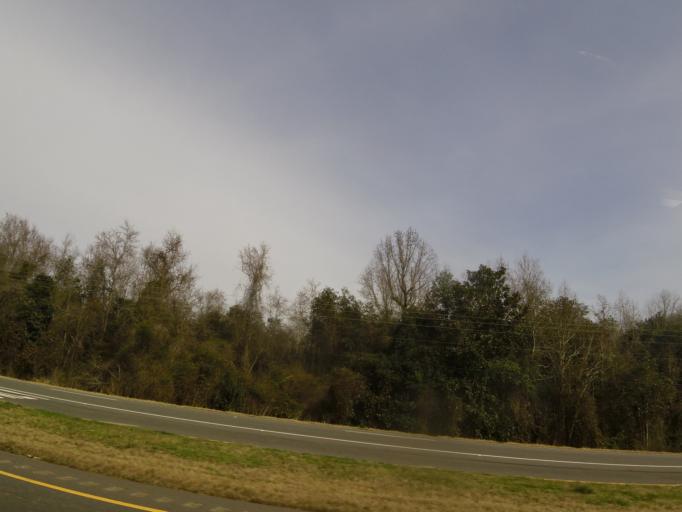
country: US
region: Alabama
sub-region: Dale County
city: Ozark
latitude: 31.4636
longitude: -85.6723
